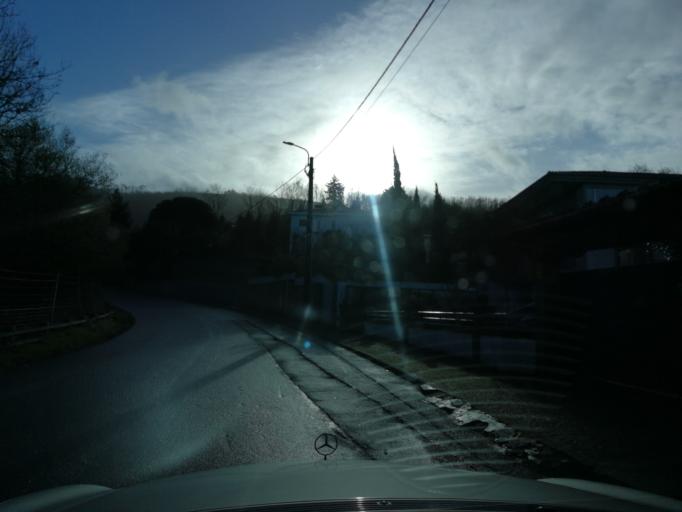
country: PT
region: Braga
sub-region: Braga
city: Braga
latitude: 41.5353
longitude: -8.3970
